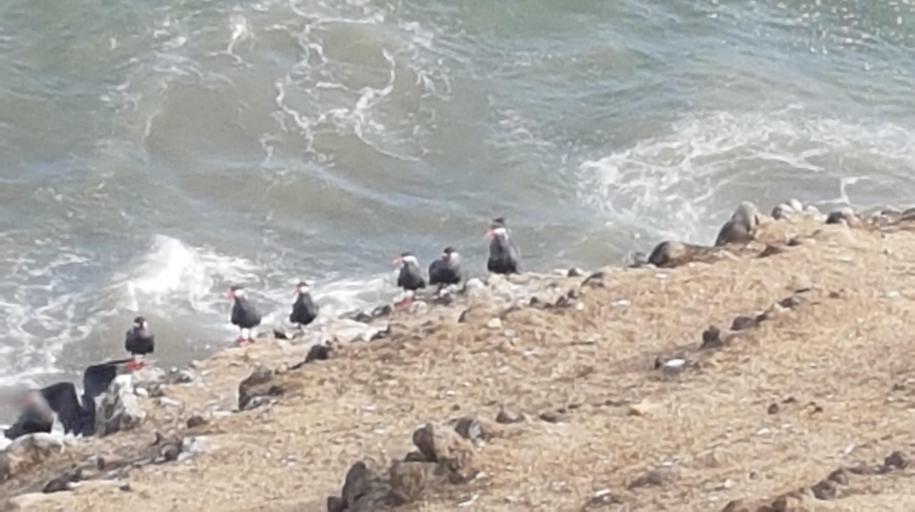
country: PE
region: Lima
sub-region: Barranca
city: Puerto Supe
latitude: -10.7997
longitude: -77.7417
